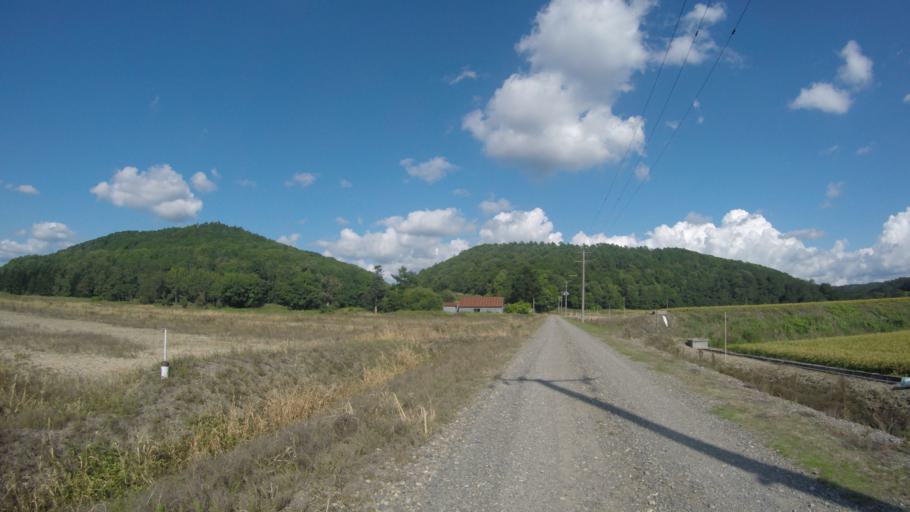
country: JP
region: Hokkaido
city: Iwamizawa
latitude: 43.1928
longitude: 141.8287
